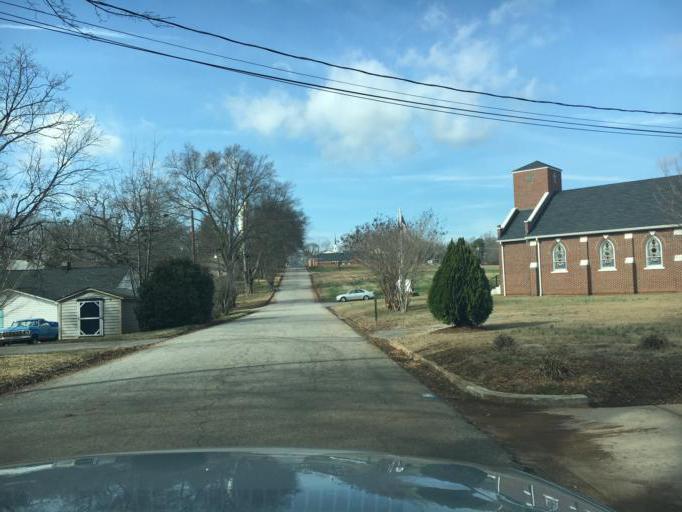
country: US
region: South Carolina
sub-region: Spartanburg County
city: Inman
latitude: 35.0410
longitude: -82.0942
